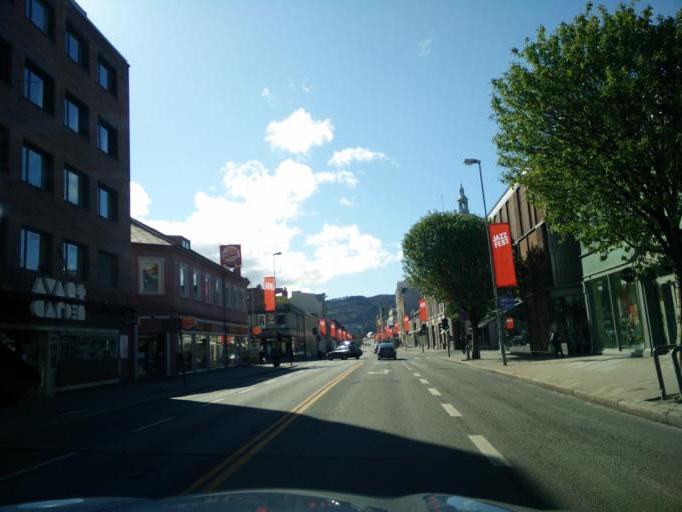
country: NO
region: Sor-Trondelag
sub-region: Trondheim
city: Trondheim
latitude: 63.4334
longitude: 10.4015
